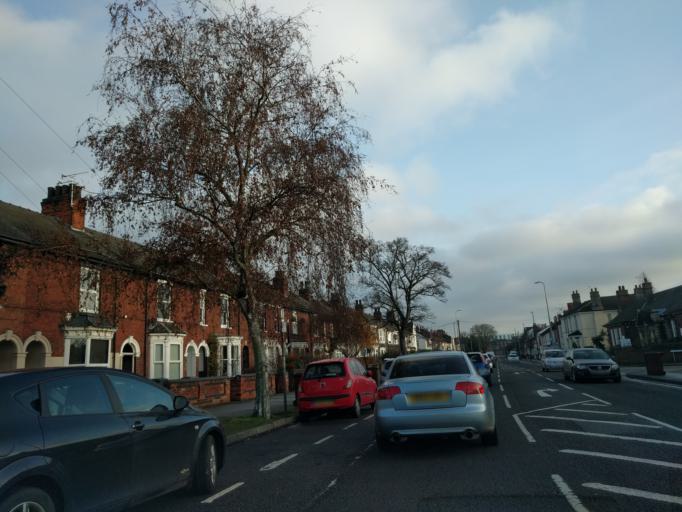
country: GB
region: England
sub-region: Lincolnshire
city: Lincoln
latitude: 53.2331
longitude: -0.5561
